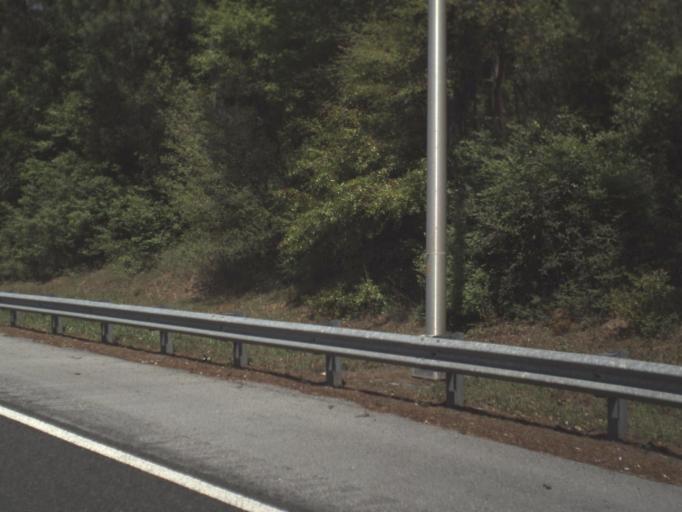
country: US
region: Florida
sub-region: Escambia County
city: Ensley
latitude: 30.5039
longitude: -87.2445
